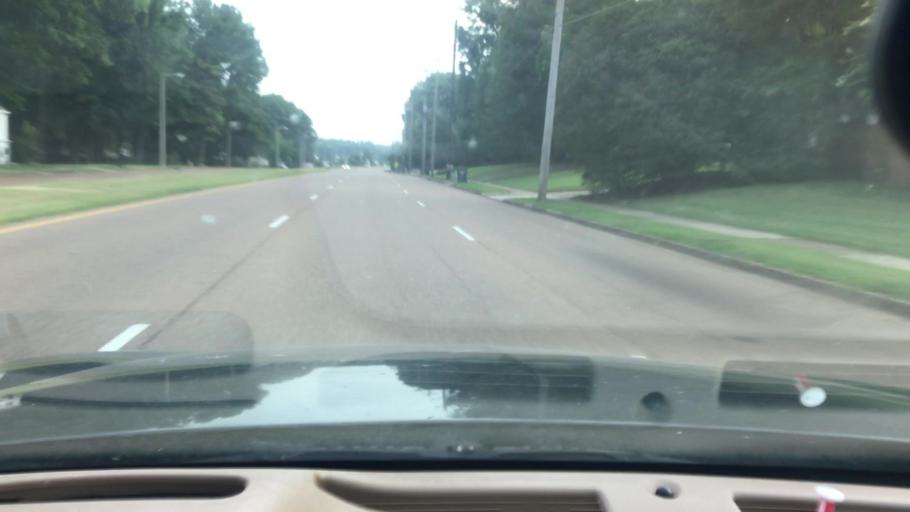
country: US
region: Tennessee
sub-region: Shelby County
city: Bartlett
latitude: 35.1939
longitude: -89.8692
